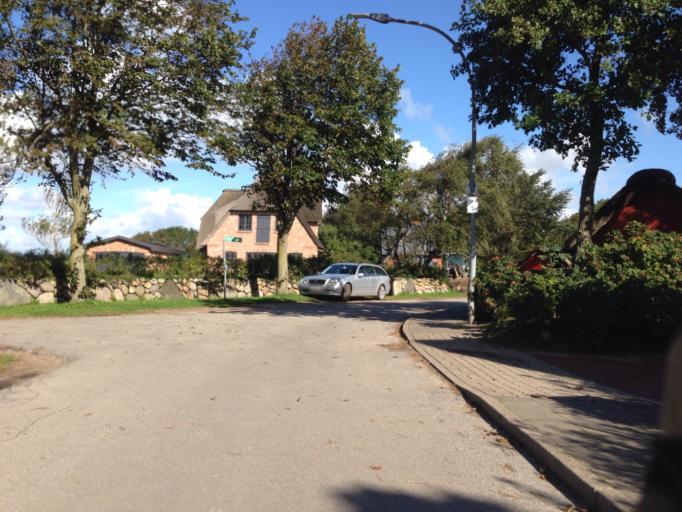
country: DE
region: Schleswig-Holstein
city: Borgsum
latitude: 54.6878
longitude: 8.4690
